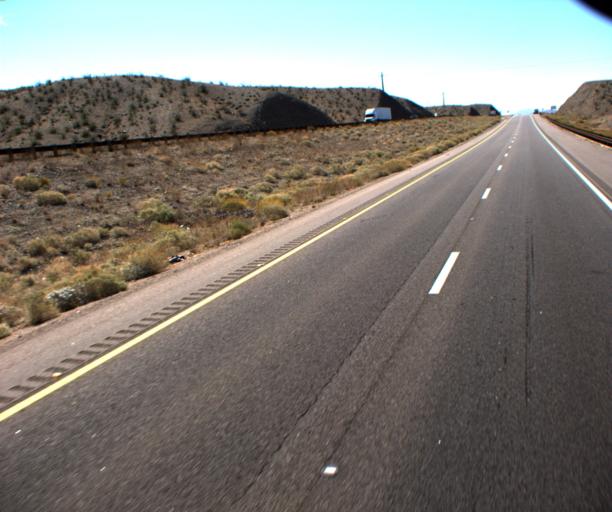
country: US
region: Nevada
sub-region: Clark County
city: Boulder City
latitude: 35.9194
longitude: -114.6312
